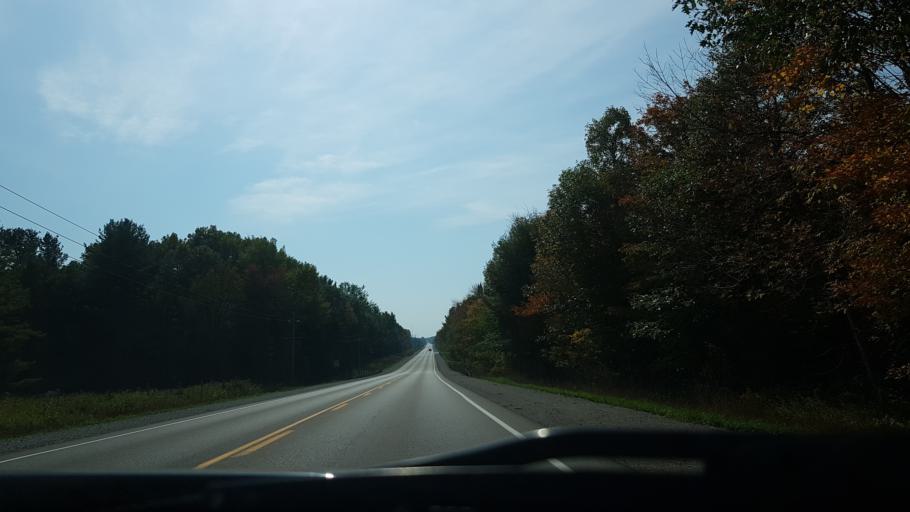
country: CA
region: Ontario
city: Orillia
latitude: 44.7228
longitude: -79.2855
